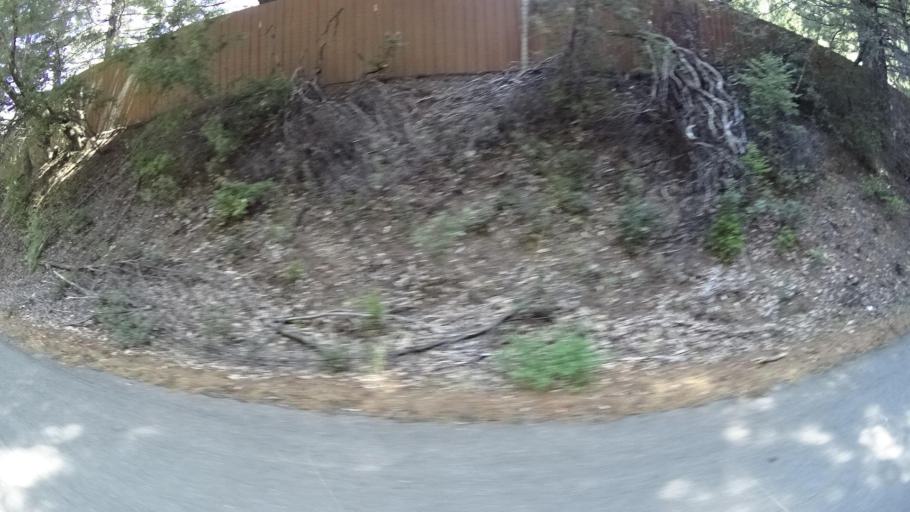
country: US
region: California
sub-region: Humboldt County
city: Redway
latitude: 40.1966
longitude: -124.0999
